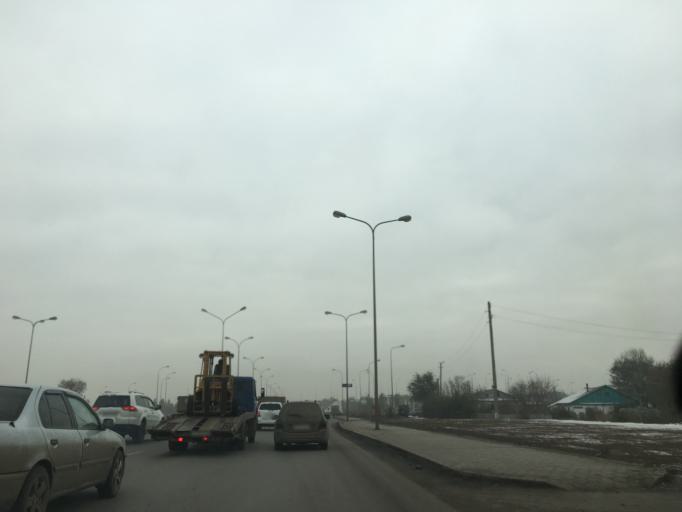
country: KZ
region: Astana Qalasy
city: Astana
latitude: 51.1756
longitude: 71.4774
